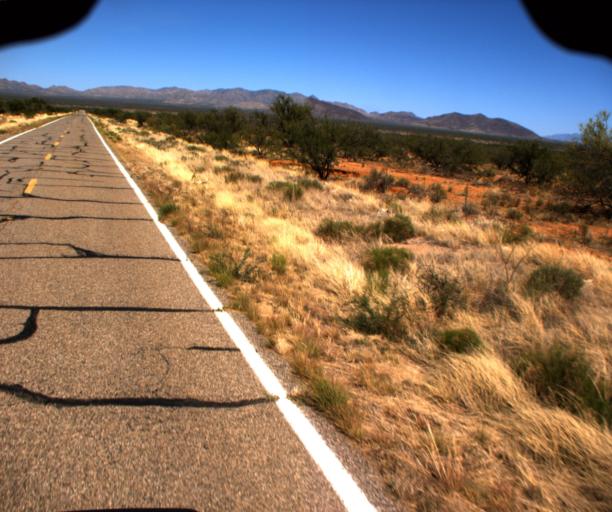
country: US
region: Arizona
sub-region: Pima County
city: Three Points
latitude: 31.8322
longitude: -111.4174
